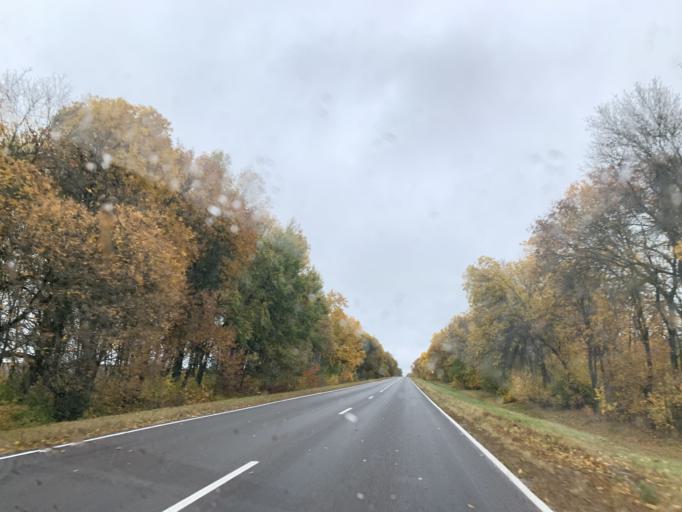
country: BY
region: Minsk
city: Haradzyeya
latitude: 53.4104
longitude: 26.6112
